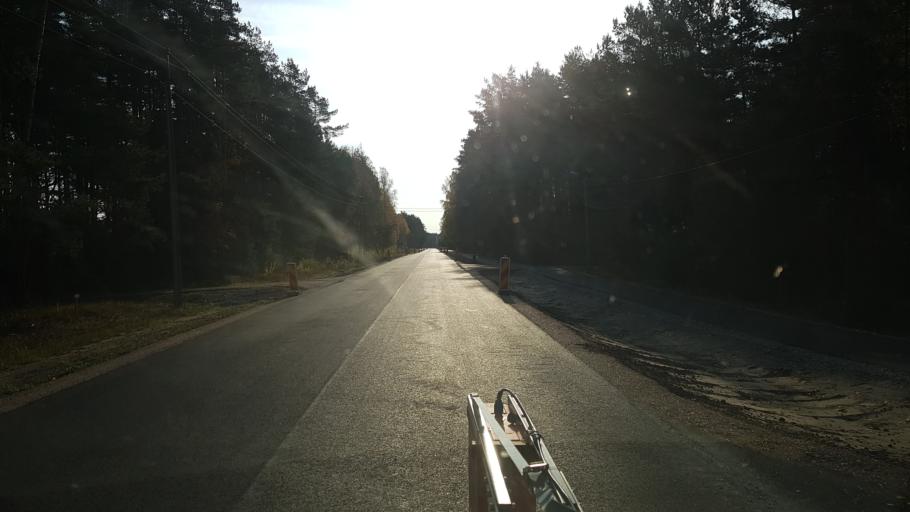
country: EE
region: Paernumaa
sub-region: Paikuse vald
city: Paikuse
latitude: 58.3610
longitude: 24.6086
